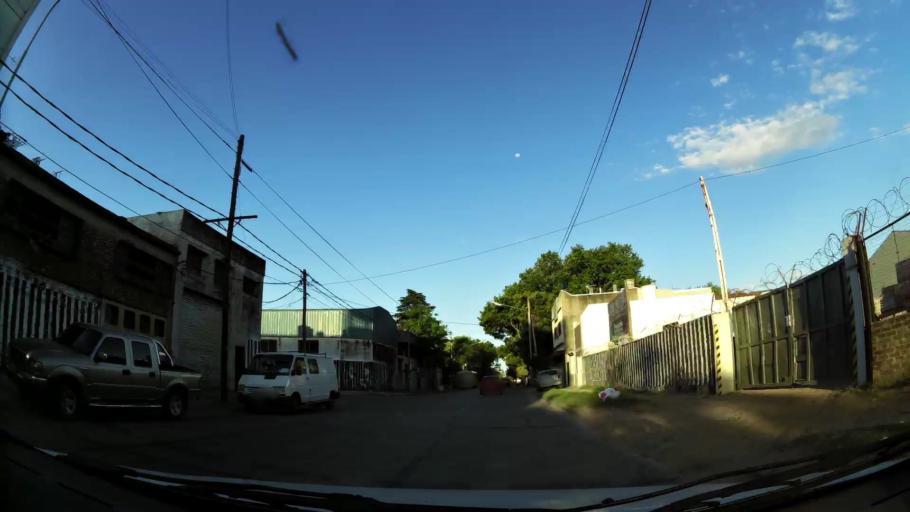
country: AR
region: Buenos Aires
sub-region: Partido de General San Martin
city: General San Martin
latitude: -34.5538
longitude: -58.5170
